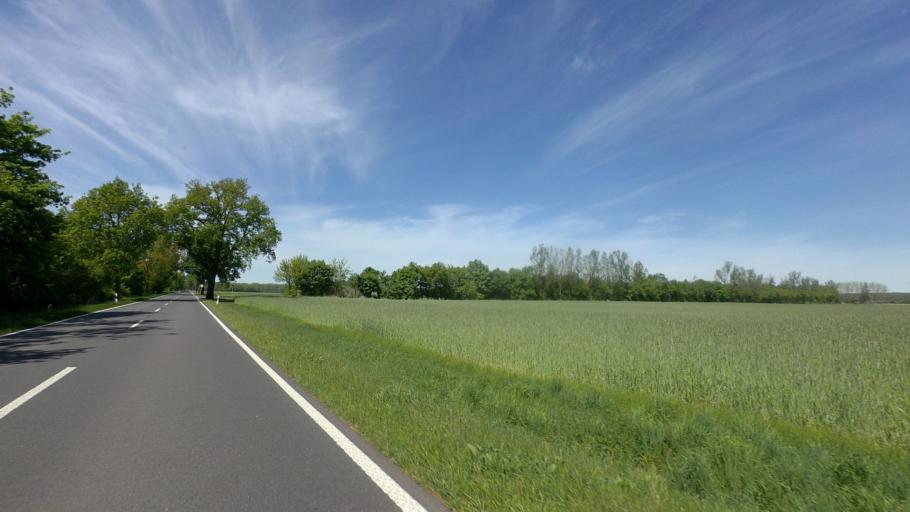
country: DE
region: Brandenburg
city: Baruth
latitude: 52.0728
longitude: 13.4621
